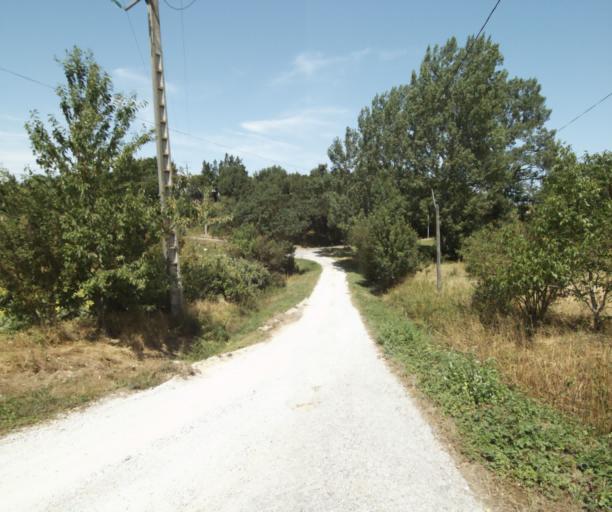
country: FR
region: Midi-Pyrenees
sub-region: Departement de la Haute-Garonne
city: Saint-Felix-Lauragais
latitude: 43.4547
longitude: 1.8450
